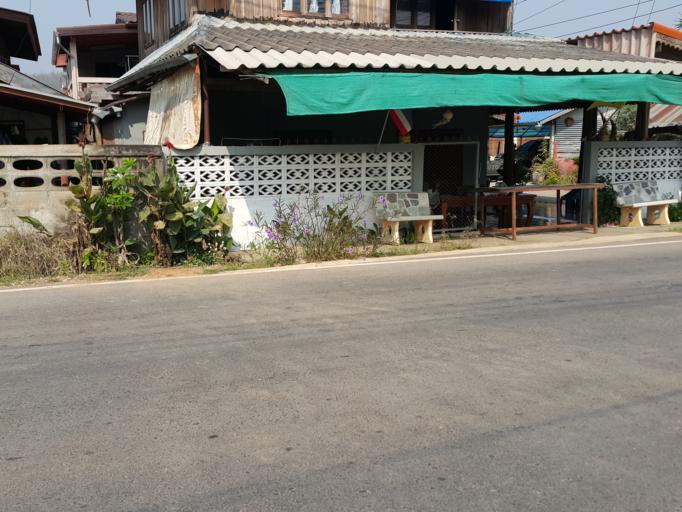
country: TH
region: Sukhothai
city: Thung Saliam
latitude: 17.3277
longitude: 99.5320
